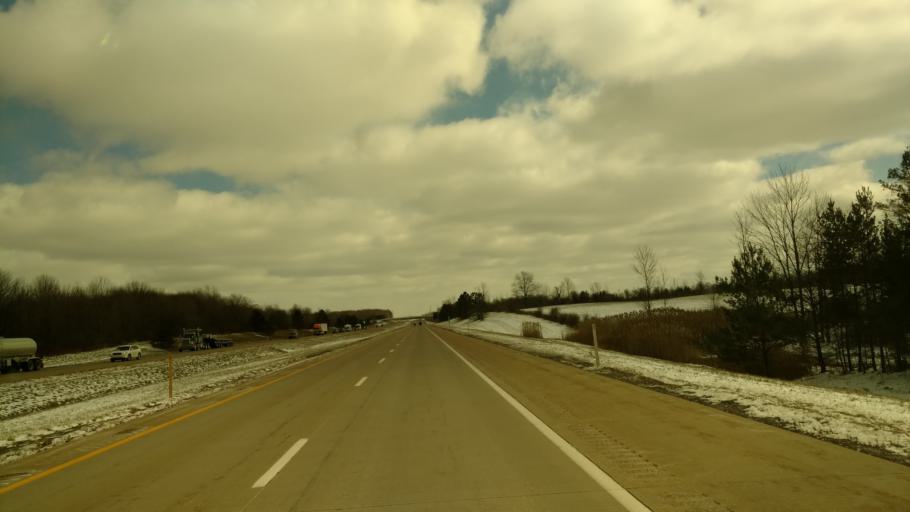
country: US
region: Ohio
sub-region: Ashtabula County
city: Geneva
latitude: 41.7706
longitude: -80.9132
